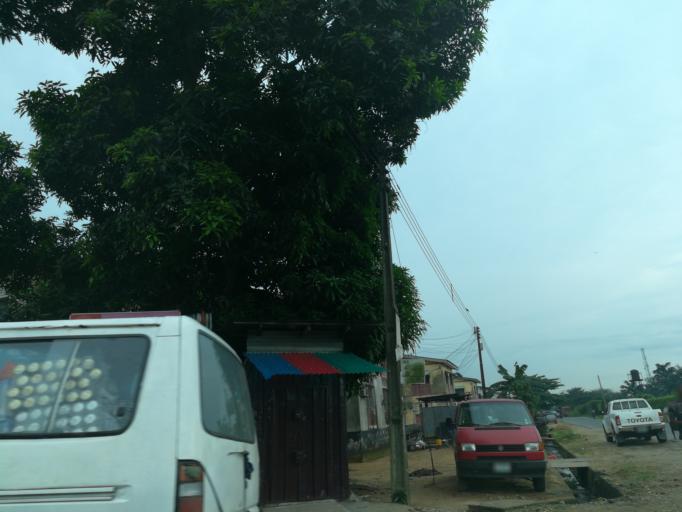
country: NG
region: Rivers
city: Port Harcourt
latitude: 4.8243
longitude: 7.0252
